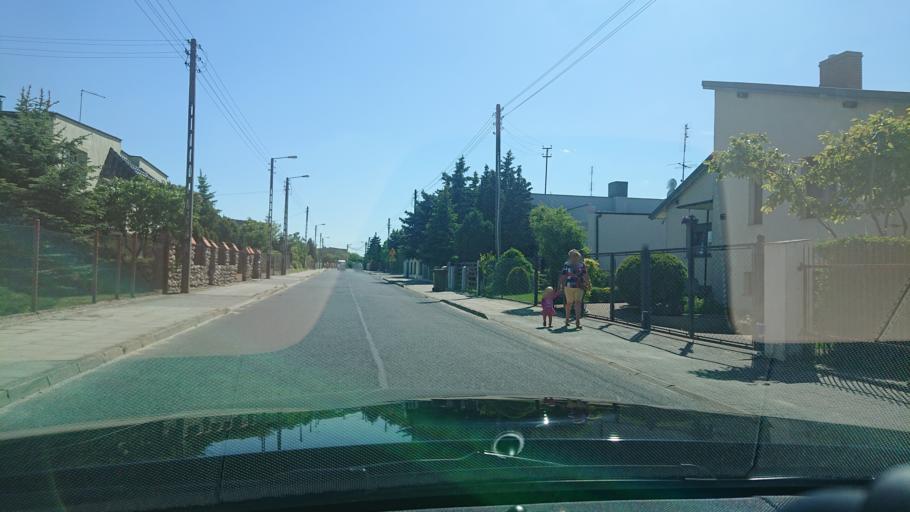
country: PL
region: Greater Poland Voivodeship
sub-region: Powiat gnieznienski
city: Gniezno
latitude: 52.5056
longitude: 17.5880
